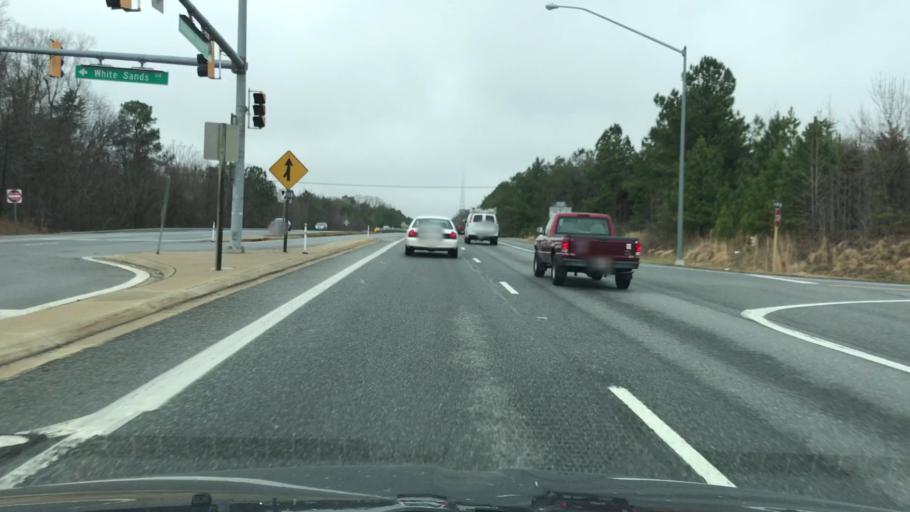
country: US
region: Maryland
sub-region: Calvert County
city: Lusby
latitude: 38.4263
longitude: -76.4633
